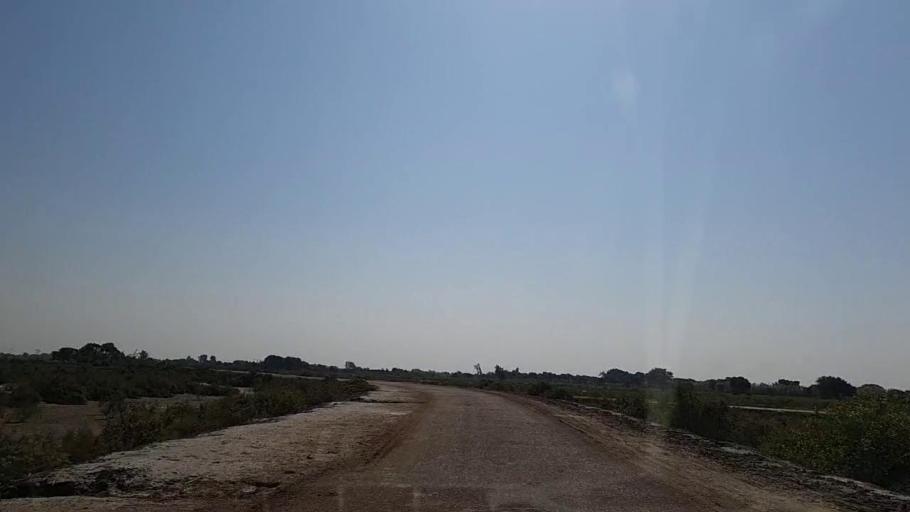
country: PK
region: Sindh
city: Chuhar Jamali
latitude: 24.5267
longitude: 68.0843
